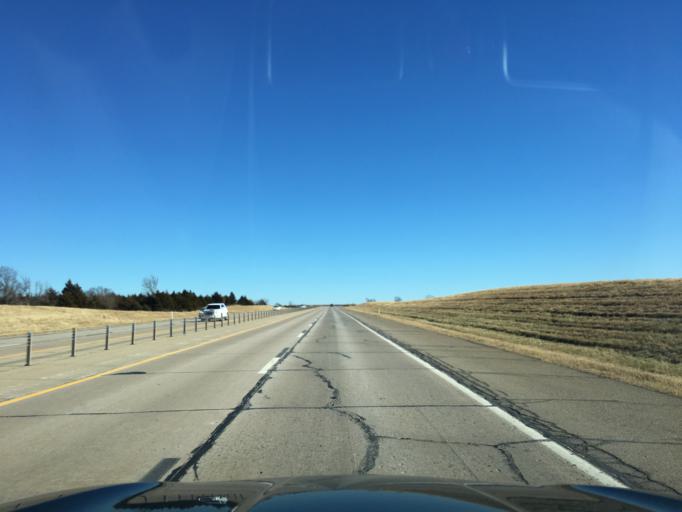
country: US
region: Oklahoma
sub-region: Pawnee County
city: Pawnee
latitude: 36.2250
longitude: -96.8475
